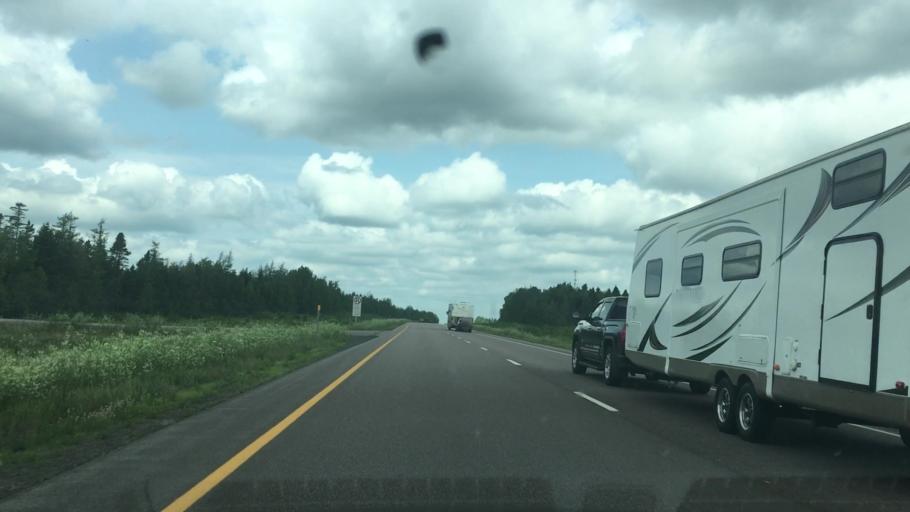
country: CA
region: New Brunswick
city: Dieppe
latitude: 46.0738
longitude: -64.5914
